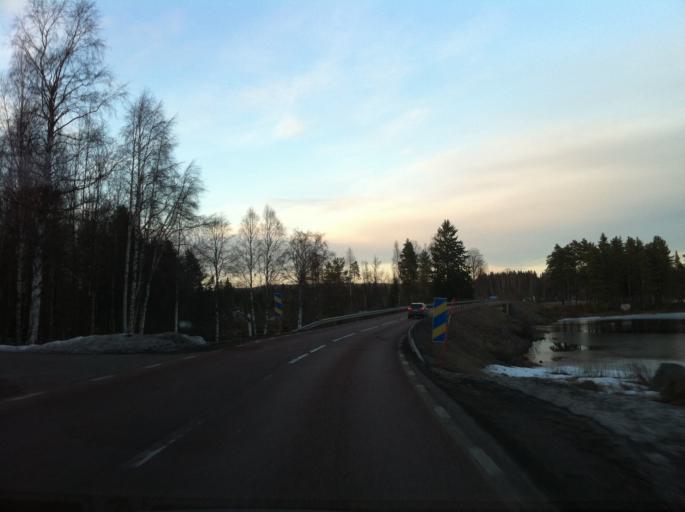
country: SE
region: Dalarna
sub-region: Vansbro Kommun
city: Vansbro
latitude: 60.8269
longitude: 14.1254
